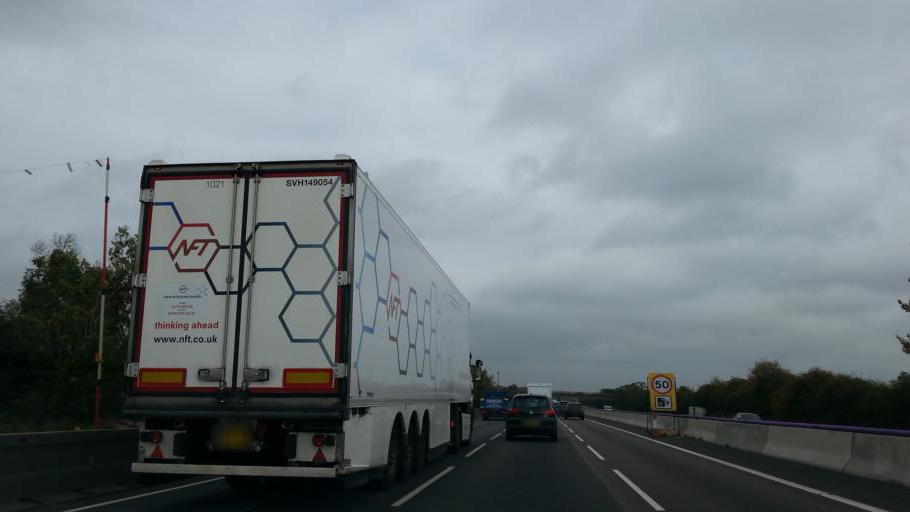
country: GB
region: England
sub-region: Cheshire East
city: Alsager
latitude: 53.1054
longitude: -2.3399
